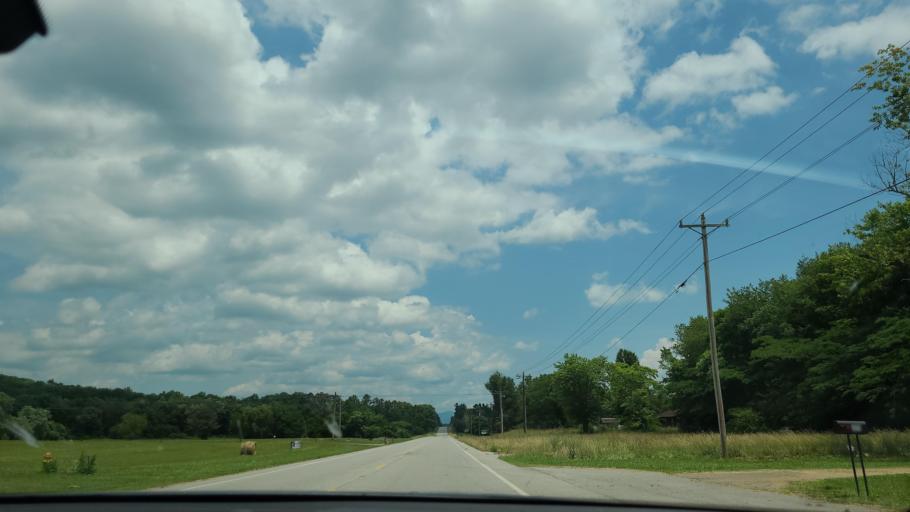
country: US
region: Tennessee
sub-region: Bledsoe County
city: Pikeville
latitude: 35.6576
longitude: -85.1525
